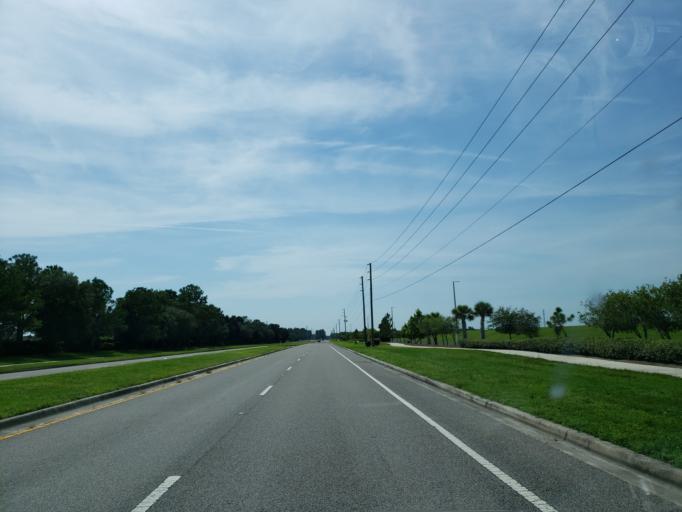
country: US
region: Florida
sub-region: Pasco County
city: Wesley Chapel
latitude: 28.2735
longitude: -82.3106
